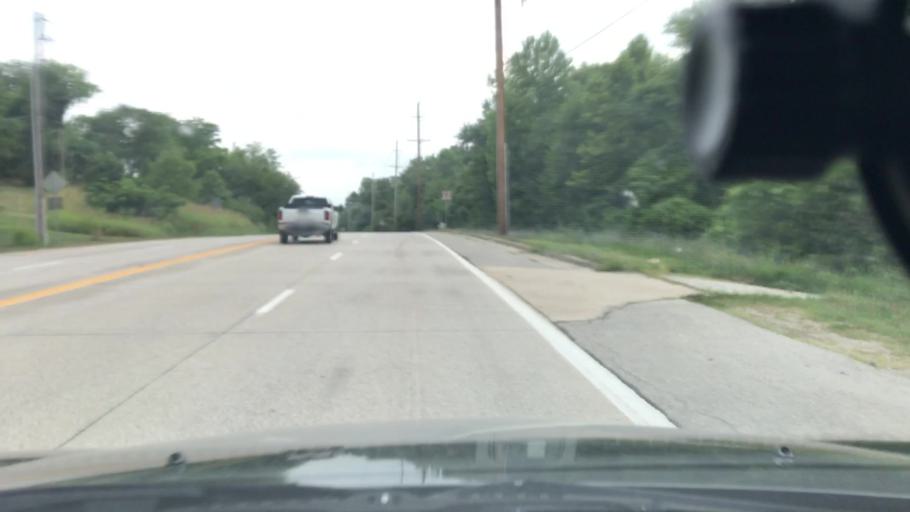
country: US
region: Missouri
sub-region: Saint Charles County
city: Saint Charles
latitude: 38.7432
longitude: -90.5174
